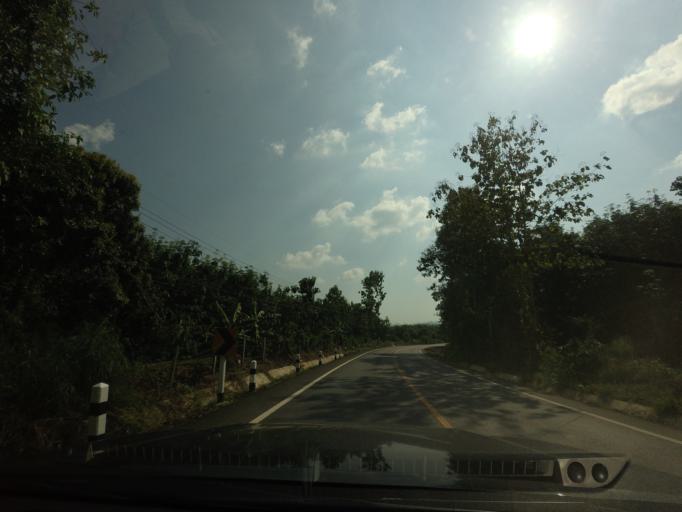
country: TH
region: Nan
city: Santi Suk
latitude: 18.9715
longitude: 100.9279
